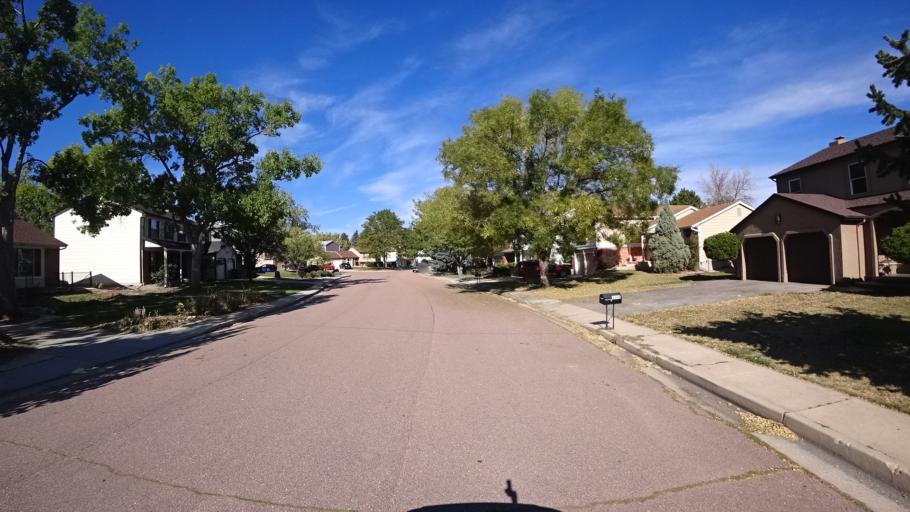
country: US
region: Colorado
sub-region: El Paso County
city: Colorado Springs
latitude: 38.9079
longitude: -104.7854
